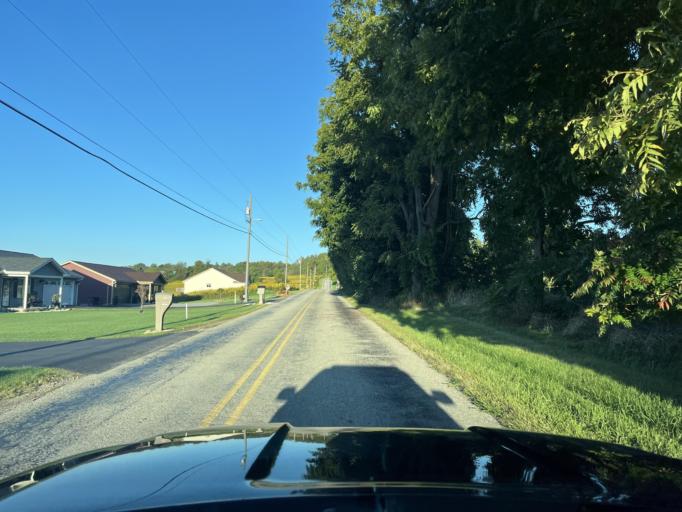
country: US
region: Pennsylvania
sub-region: Fayette County
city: Leith-Hatfield
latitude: 39.8684
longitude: -79.7328
